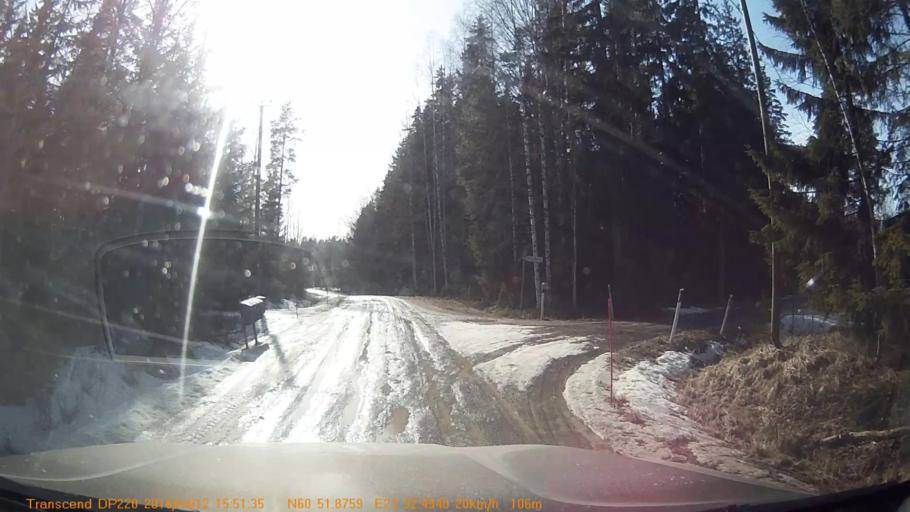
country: FI
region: Haeme
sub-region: Forssa
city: Jokioinen
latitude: 60.8646
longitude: 23.5404
